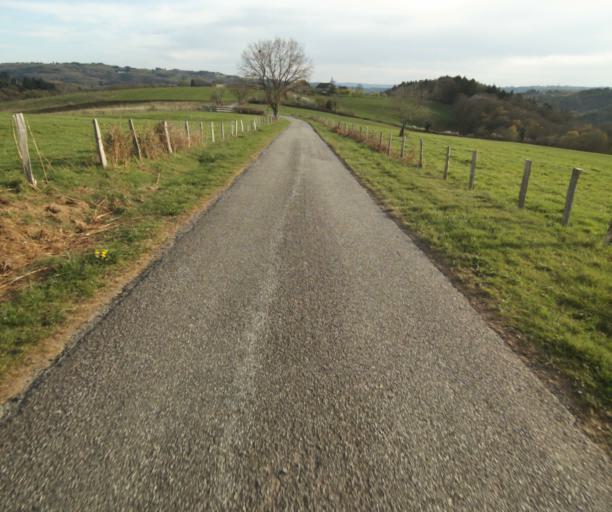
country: FR
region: Limousin
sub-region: Departement de la Correze
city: Correze
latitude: 45.3689
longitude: 1.8328
